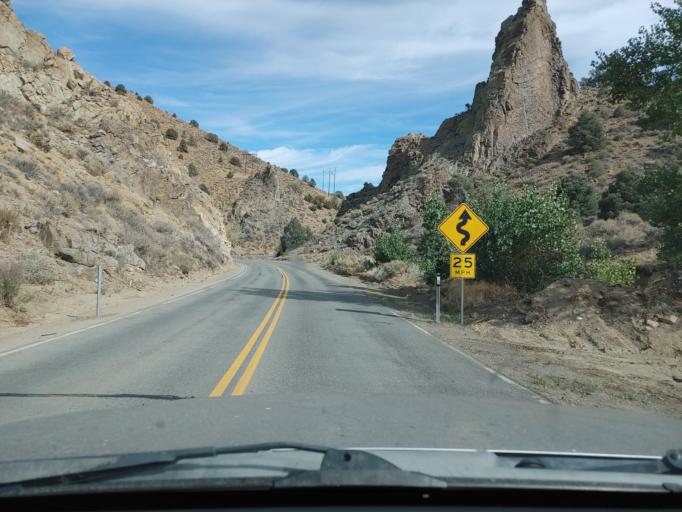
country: US
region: Nevada
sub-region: Storey County
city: Virginia City
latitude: 39.3153
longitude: -119.5948
